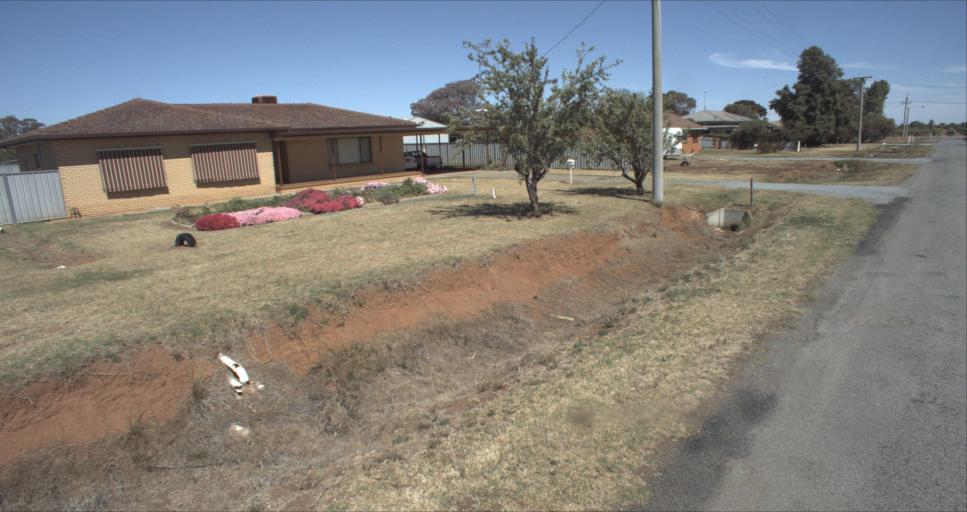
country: AU
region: New South Wales
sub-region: Leeton
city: Leeton
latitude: -34.5533
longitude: 146.3806
